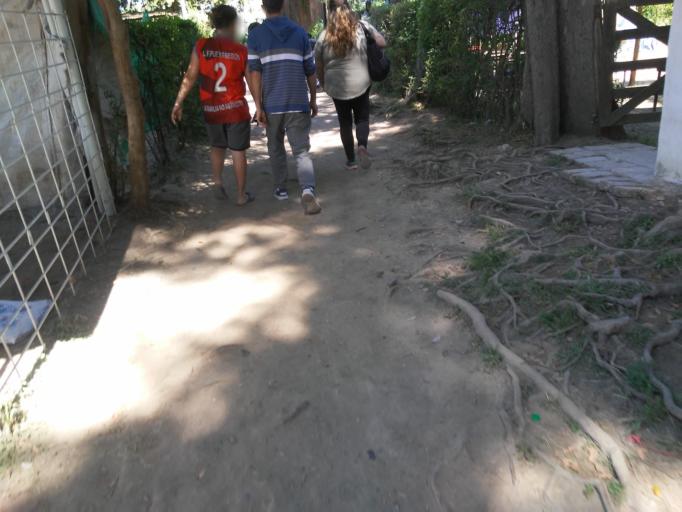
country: AR
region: Buenos Aires
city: Belen de Escobar
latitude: -34.2460
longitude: -58.7372
